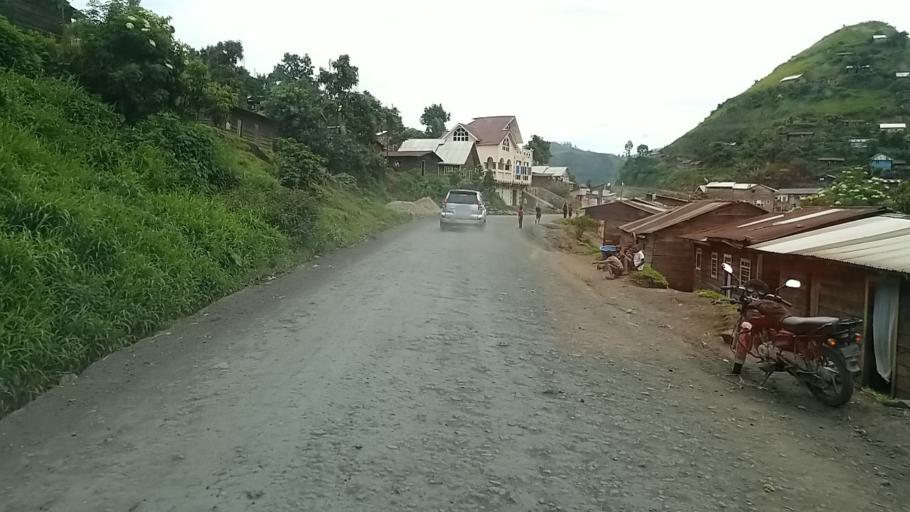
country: CD
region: Nord Kivu
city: Sake
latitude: -1.7553
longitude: 28.9854
